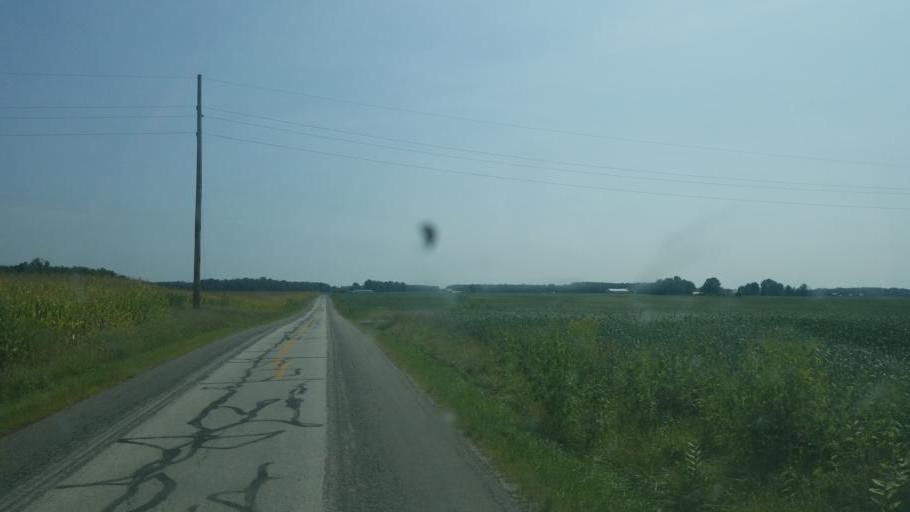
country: US
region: Ohio
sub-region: Crawford County
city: Crestline
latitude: 40.8369
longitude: -82.7445
